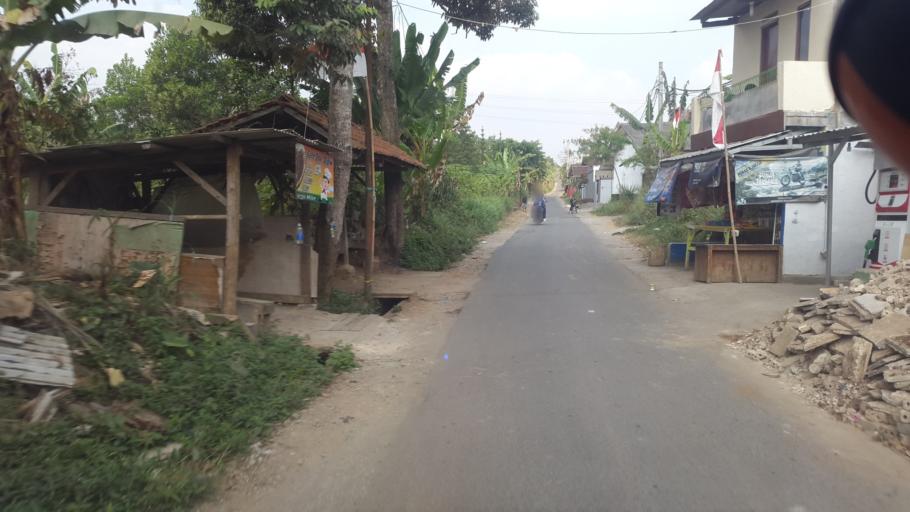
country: ID
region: West Java
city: Cicurug
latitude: -6.7654
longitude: 106.8090
